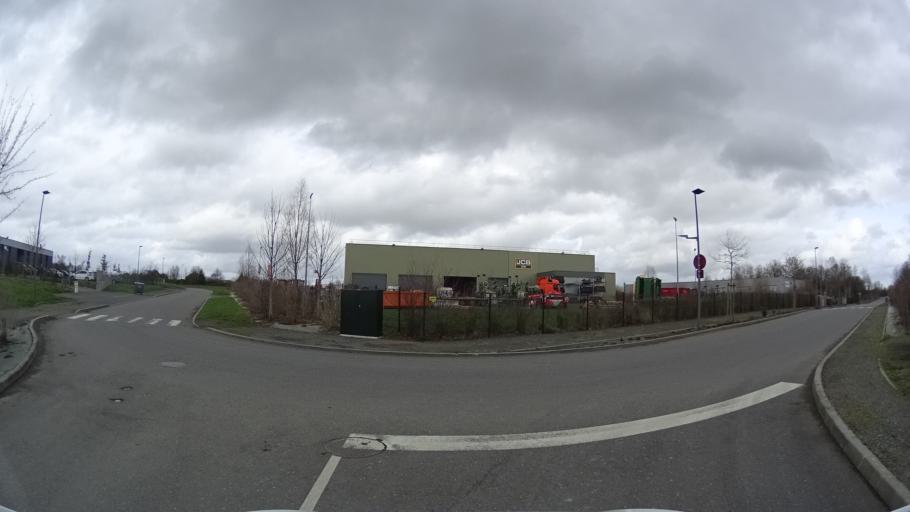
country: FR
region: Brittany
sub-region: Departement d'Ille-et-Vilaine
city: Saint-Gilles
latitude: 48.1577
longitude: -1.8302
